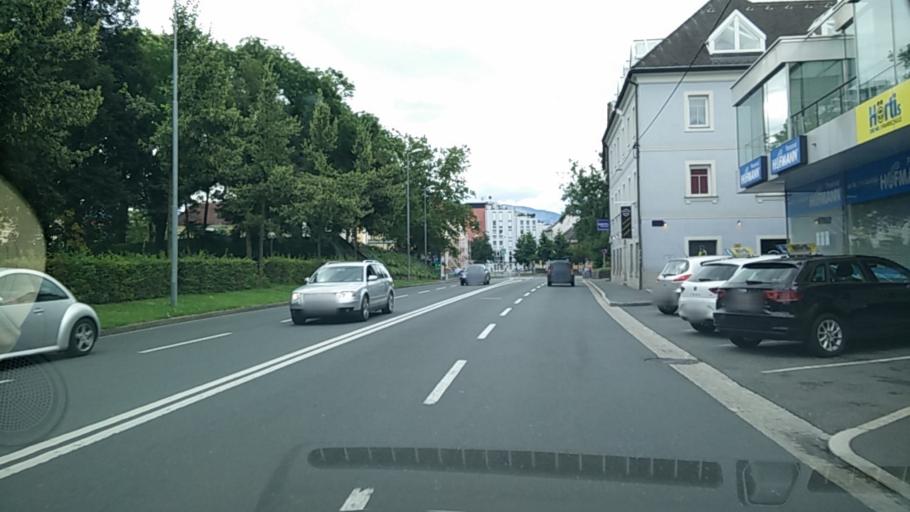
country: AT
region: Carinthia
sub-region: Klagenfurt am Woerthersee
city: Klagenfurt am Woerthersee
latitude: 46.6253
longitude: 14.3026
